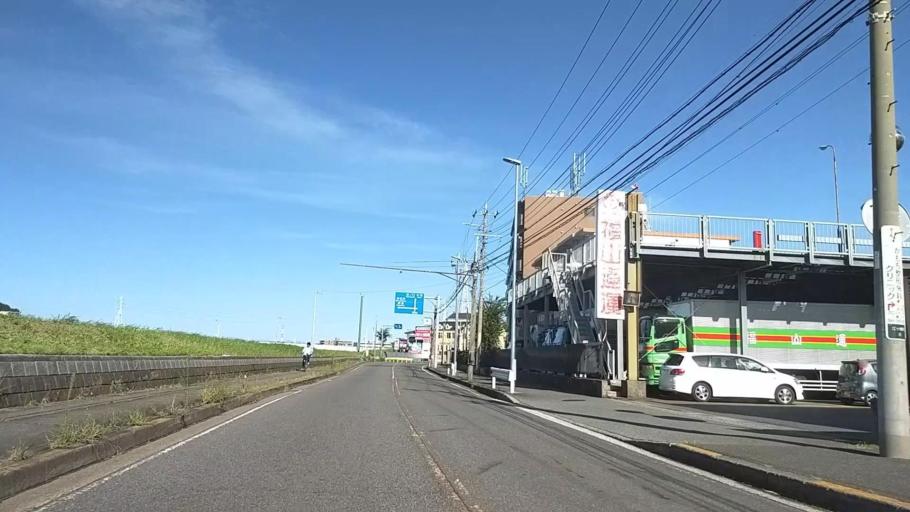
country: JP
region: Kanagawa
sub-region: Kawasaki-shi
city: Kawasaki
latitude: 35.5329
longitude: 139.6684
